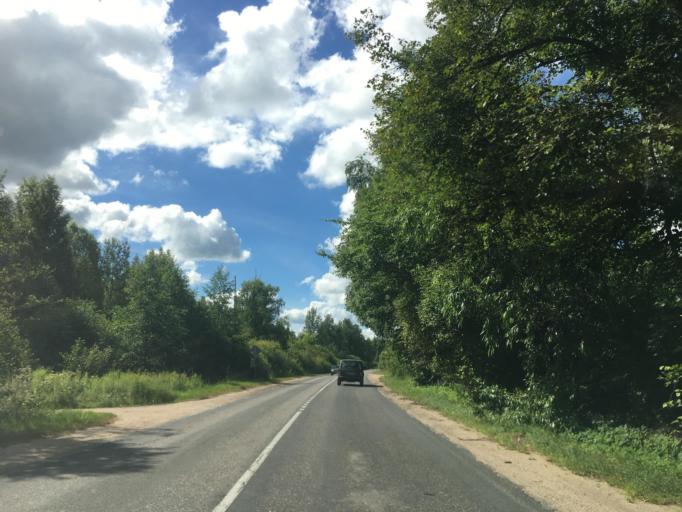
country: RU
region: Pskov
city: Pskov
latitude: 57.6947
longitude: 28.1794
